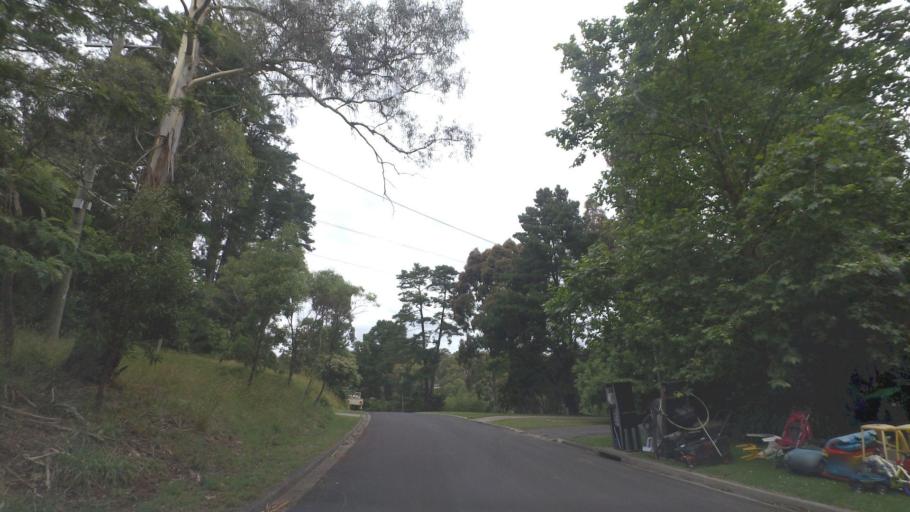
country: AU
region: Victoria
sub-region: Manningham
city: Park Orchards
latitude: -37.7840
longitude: 145.2139
